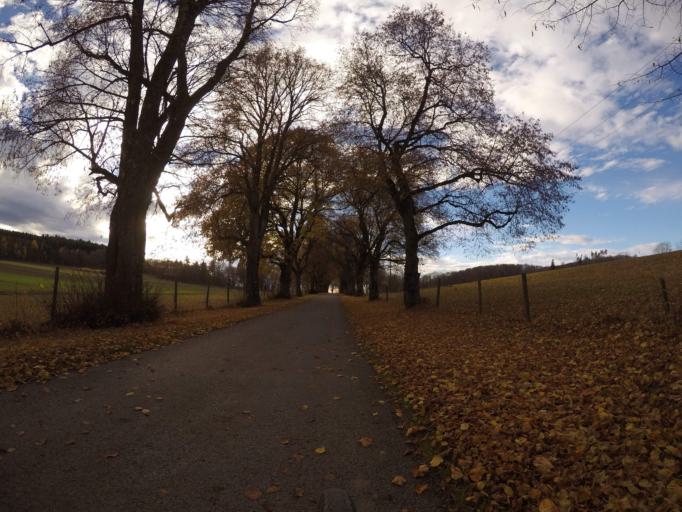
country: DE
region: Baden-Wuerttemberg
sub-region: Tuebingen Region
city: Sankt Johann
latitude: 48.4731
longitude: 9.3031
